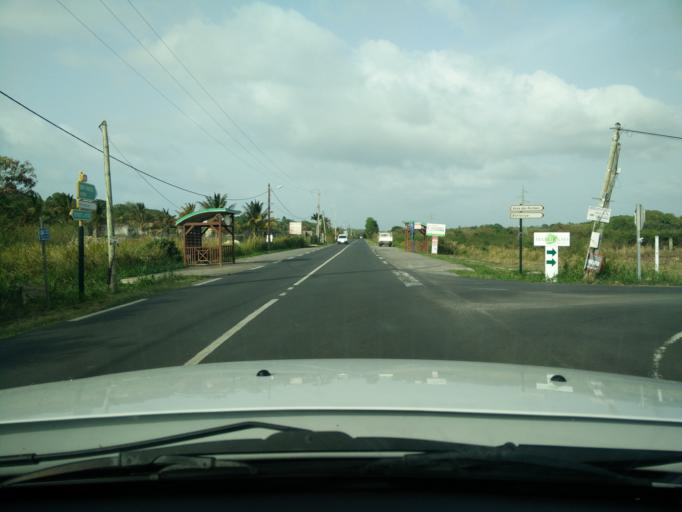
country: GP
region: Guadeloupe
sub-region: Guadeloupe
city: Saint-Francois
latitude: 16.2569
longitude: -61.3089
